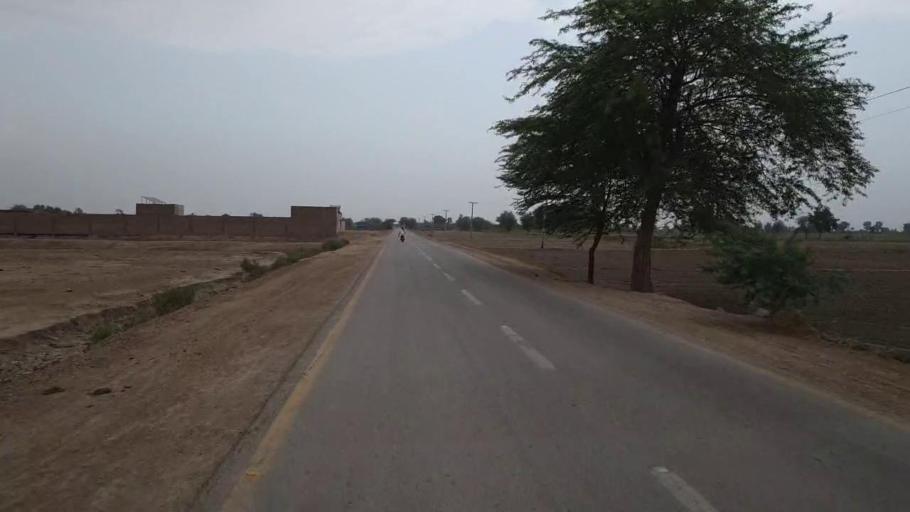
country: PK
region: Sindh
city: Bandhi
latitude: 26.5905
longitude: 68.2001
